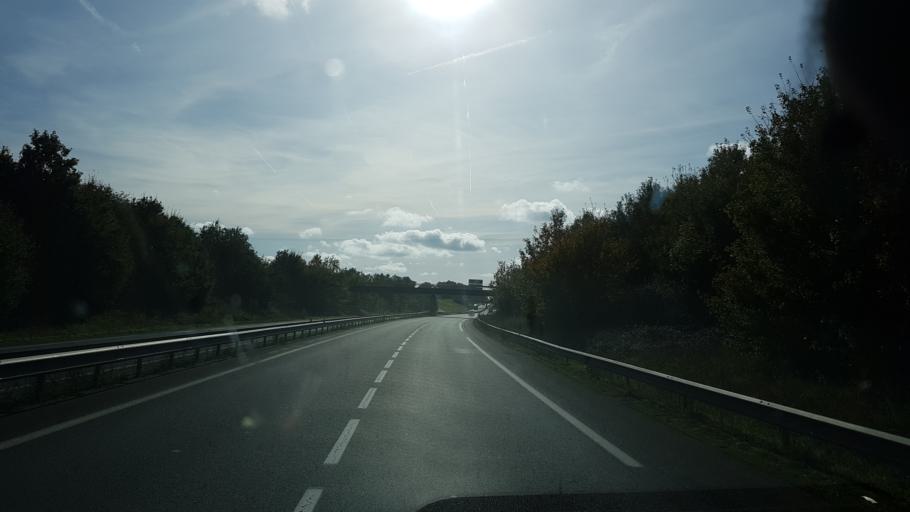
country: FR
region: Poitou-Charentes
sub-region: Departement de la Charente
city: Chasseneuil-sur-Bonnieure
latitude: 45.8170
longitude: 0.4550
